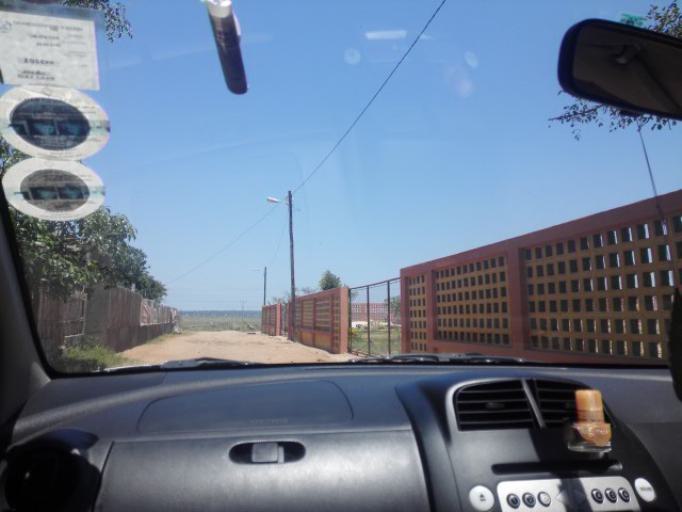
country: MZ
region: Maputo City
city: Maputo
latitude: -25.7392
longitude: 32.7306
